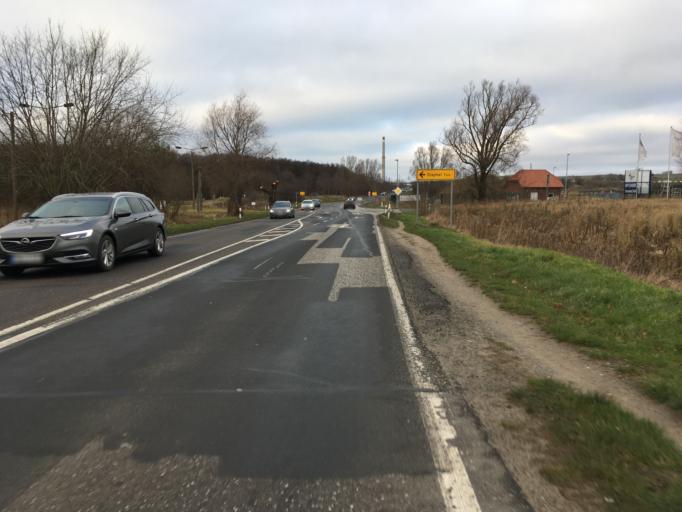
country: DE
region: Mecklenburg-Vorpommern
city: Sagard
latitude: 54.4833
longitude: 13.5784
